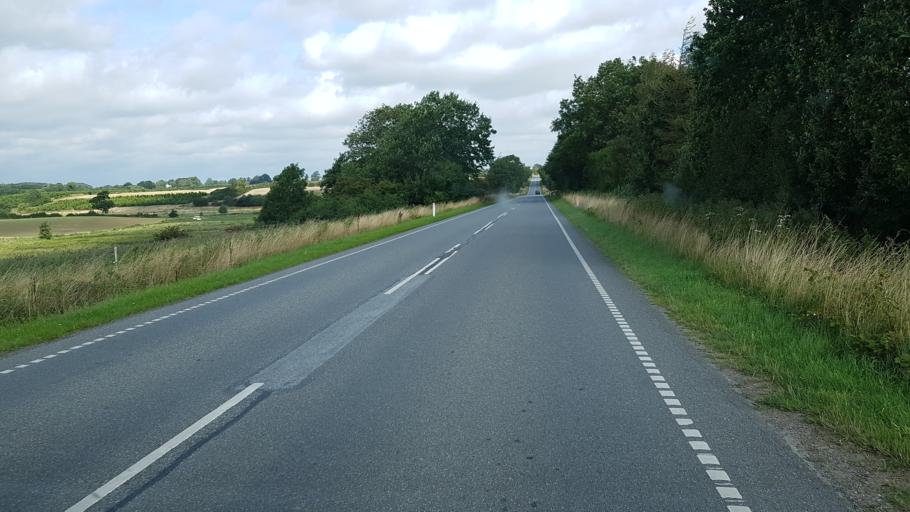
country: DK
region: South Denmark
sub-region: Haderslev Kommune
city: Starup
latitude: 55.3062
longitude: 9.5608
